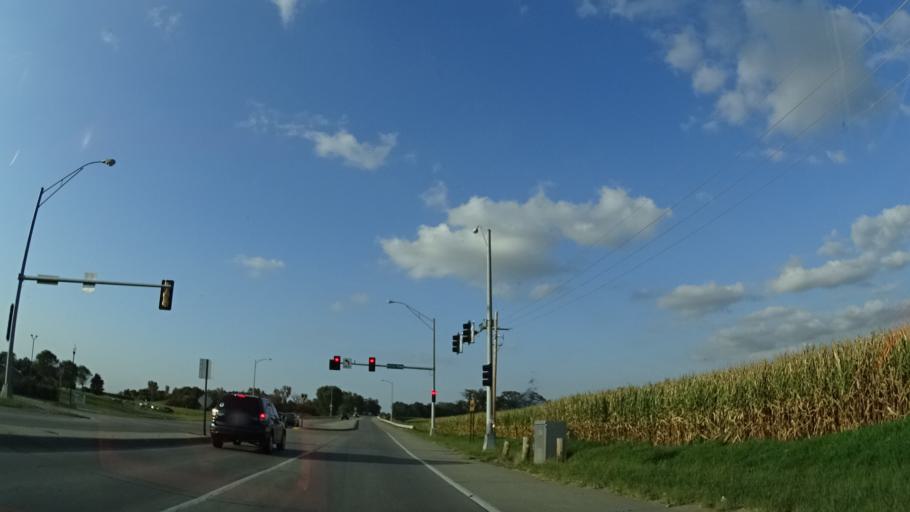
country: US
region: Nebraska
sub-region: Sarpy County
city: Offutt Air Force Base
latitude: 41.1470
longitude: -95.9668
